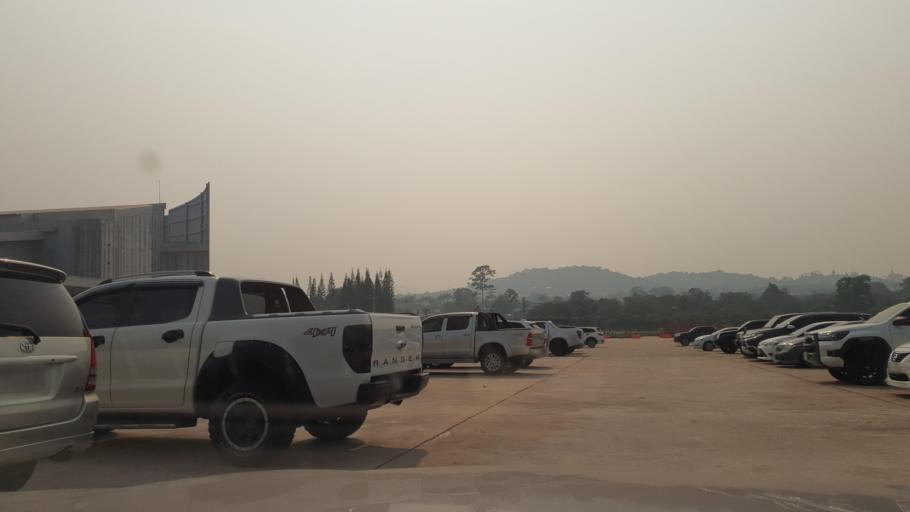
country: TH
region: Chon Buri
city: Sattahip
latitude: 12.7694
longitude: 100.9342
